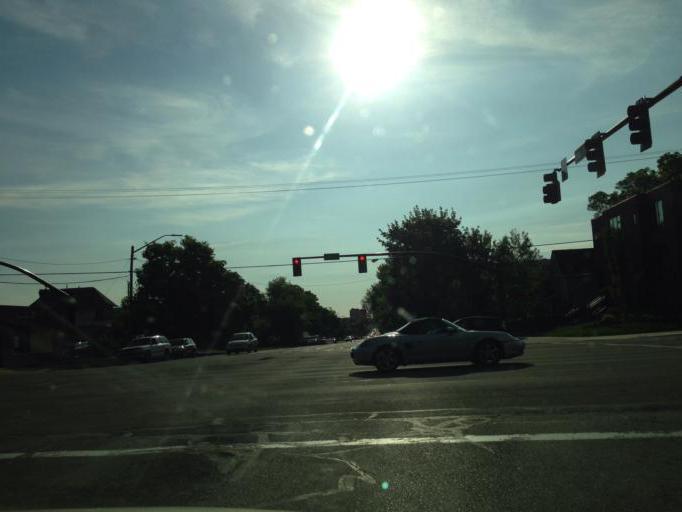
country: US
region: Utah
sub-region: Salt Lake County
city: Salt Lake City
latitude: 40.7628
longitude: -111.8708
